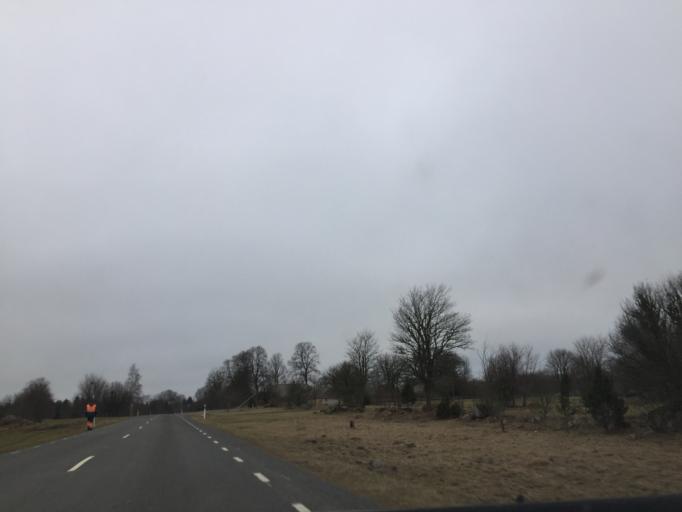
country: EE
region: Saare
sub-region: Kuressaare linn
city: Kuressaare
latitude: 58.5363
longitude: 22.3391
